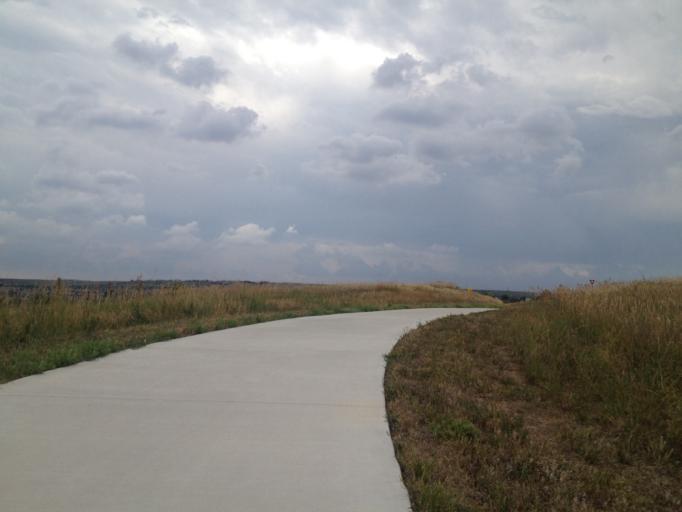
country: US
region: Colorado
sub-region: Boulder County
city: Superior
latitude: 39.9496
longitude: -105.1472
